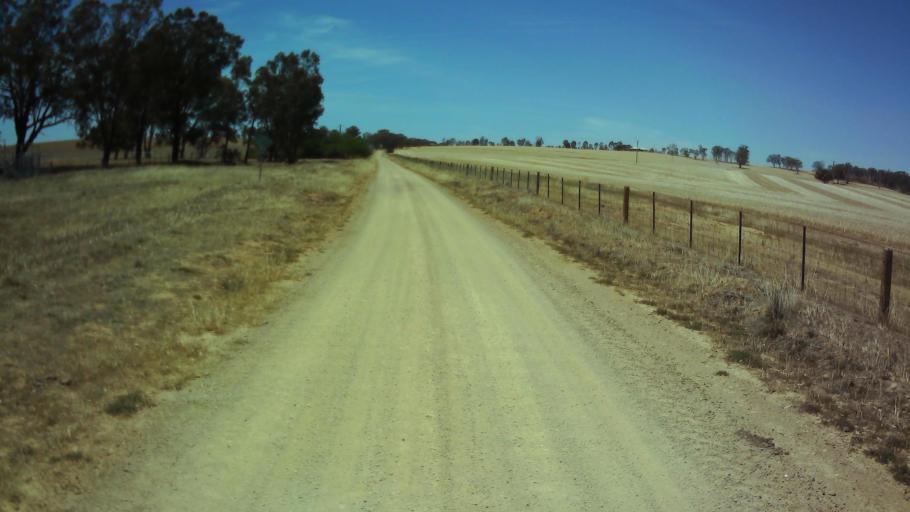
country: AU
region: New South Wales
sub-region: Weddin
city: Grenfell
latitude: -33.9301
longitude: 148.1623
